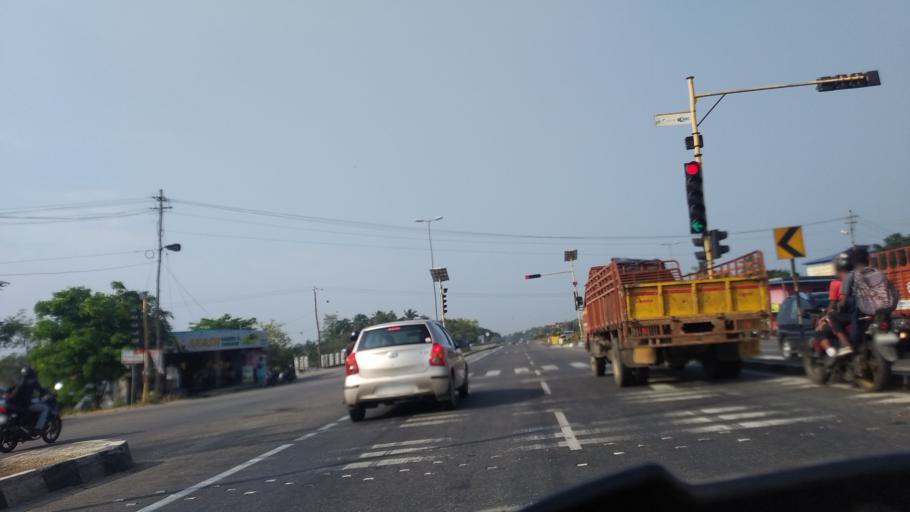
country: IN
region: Kerala
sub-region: Palakkad district
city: Palakkad
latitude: 10.7362
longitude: 76.6173
